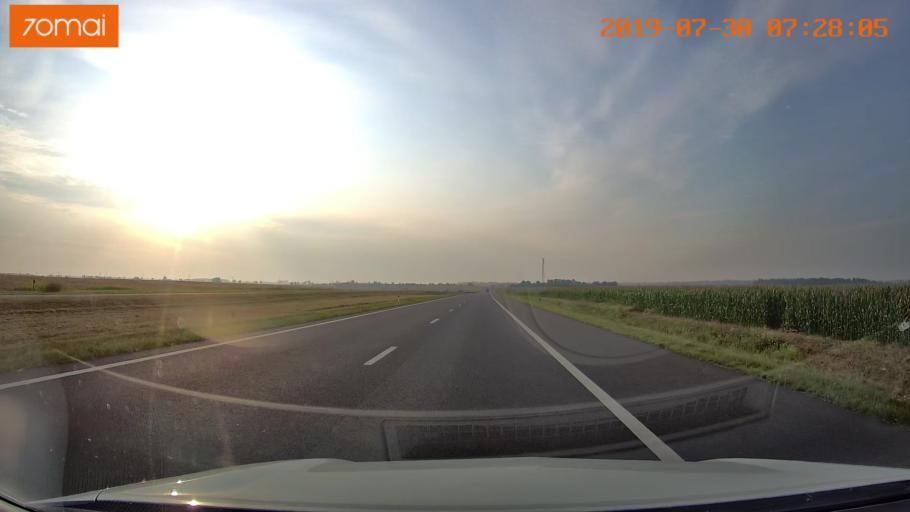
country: RU
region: Kaliningrad
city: Gvardeysk
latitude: 54.6792
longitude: 20.9037
